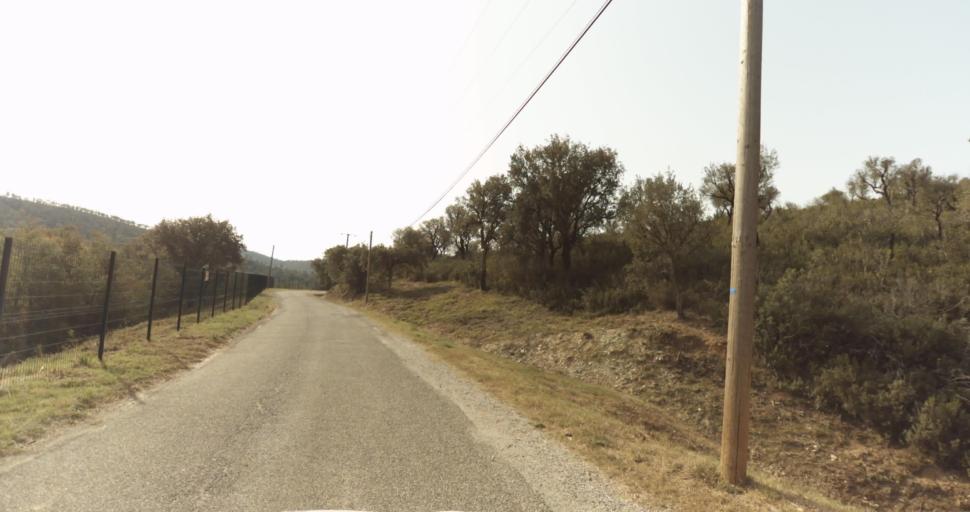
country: FR
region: Provence-Alpes-Cote d'Azur
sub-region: Departement du Var
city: Bormes-les-Mimosas
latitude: 43.1476
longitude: 6.2923
